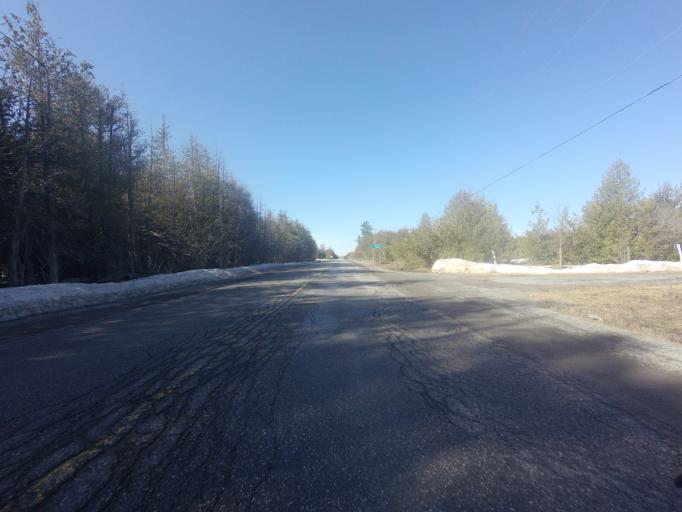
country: CA
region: Ontario
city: Carleton Place
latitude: 45.2033
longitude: -75.9841
